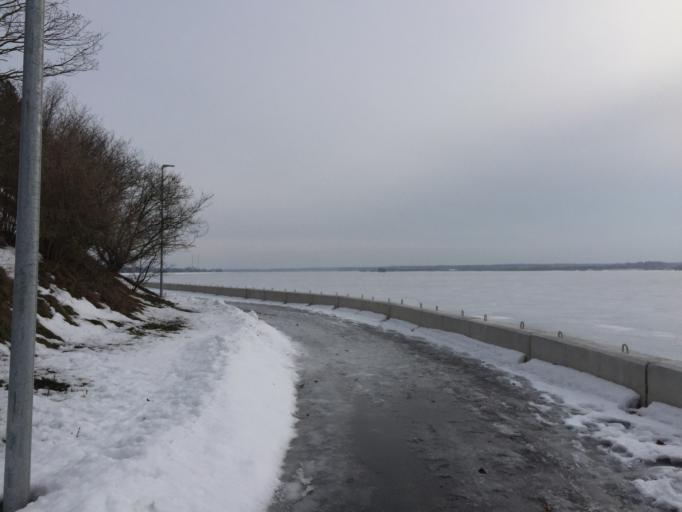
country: LV
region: Ikskile
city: Ikskile
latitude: 56.8436
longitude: 24.4528
